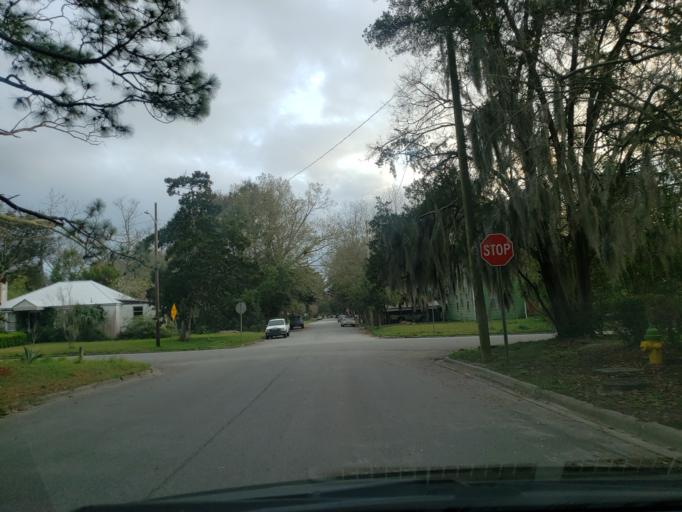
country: US
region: Georgia
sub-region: Chatham County
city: Thunderbolt
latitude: 32.0356
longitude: -81.0967
